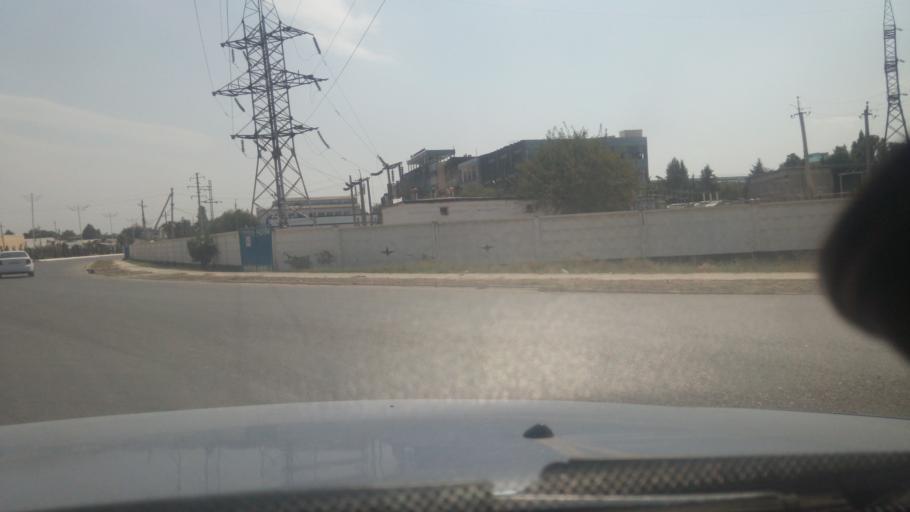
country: UZ
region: Sirdaryo
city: Guliston
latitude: 40.5207
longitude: 68.7674
